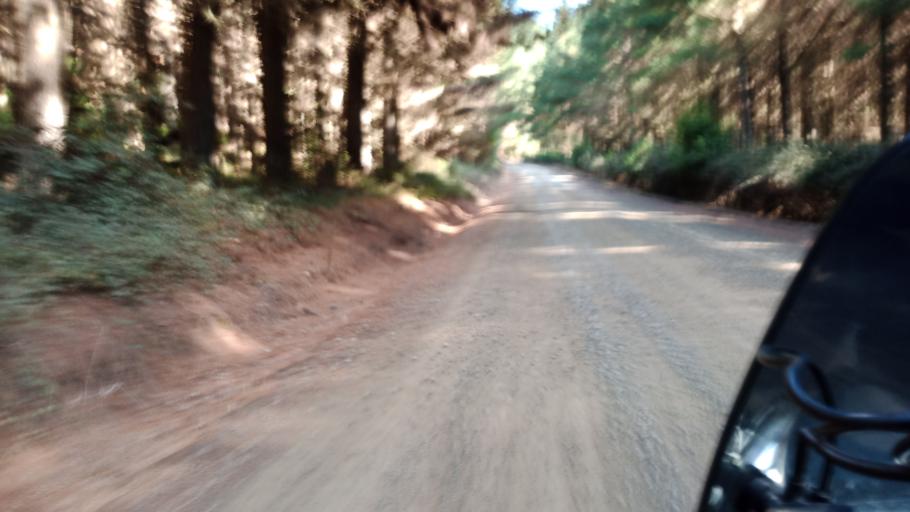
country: NZ
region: Hawke's Bay
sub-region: Wairoa District
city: Wairoa
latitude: -38.9320
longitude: 177.2311
